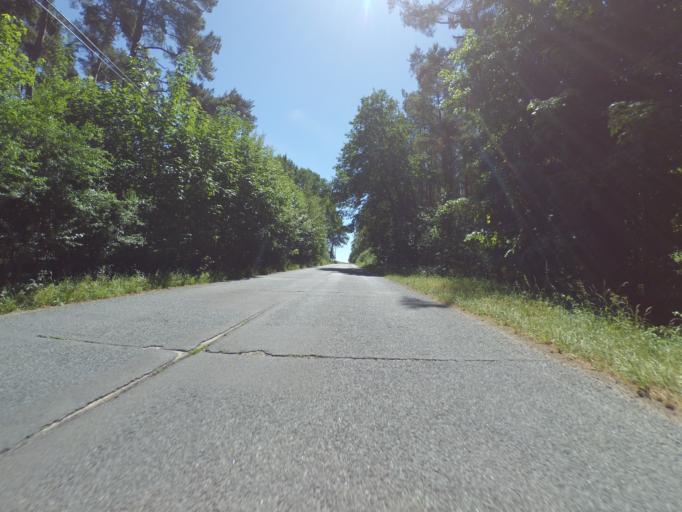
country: DE
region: Mecklenburg-Vorpommern
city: Plau am See
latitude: 53.4218
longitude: 12.3244
